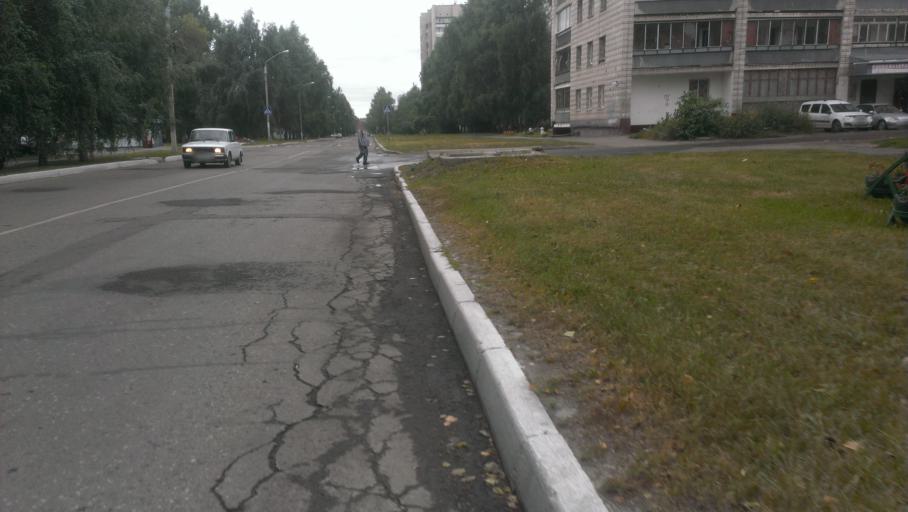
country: RU
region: Altai Krai
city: Novosilikatnyy
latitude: 53.3718
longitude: 83.6697
